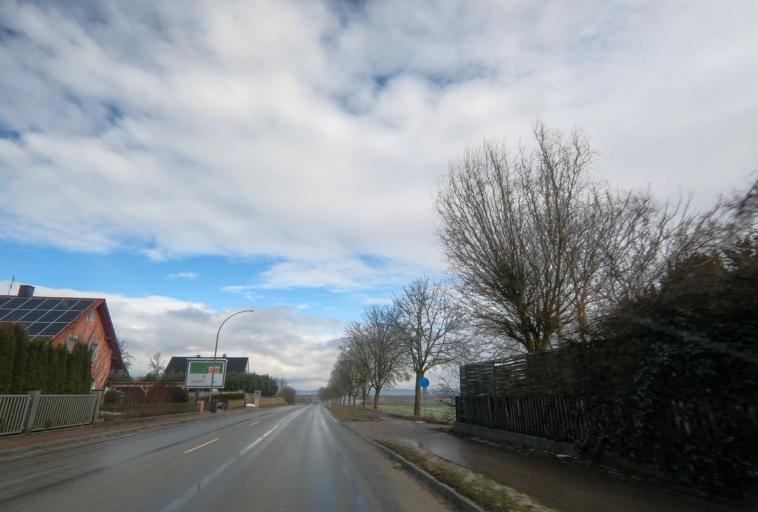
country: DE
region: Bavaria
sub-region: Upper Palatinate
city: Hagelstadt
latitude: 48.9002
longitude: 12.2130
